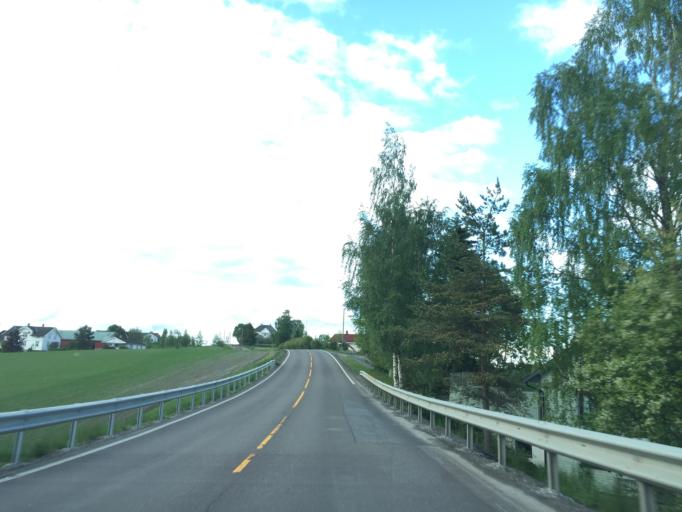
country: NO
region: Akershus
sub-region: Sorum
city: Sorumsand
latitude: 59.9719
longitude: 11.2242
